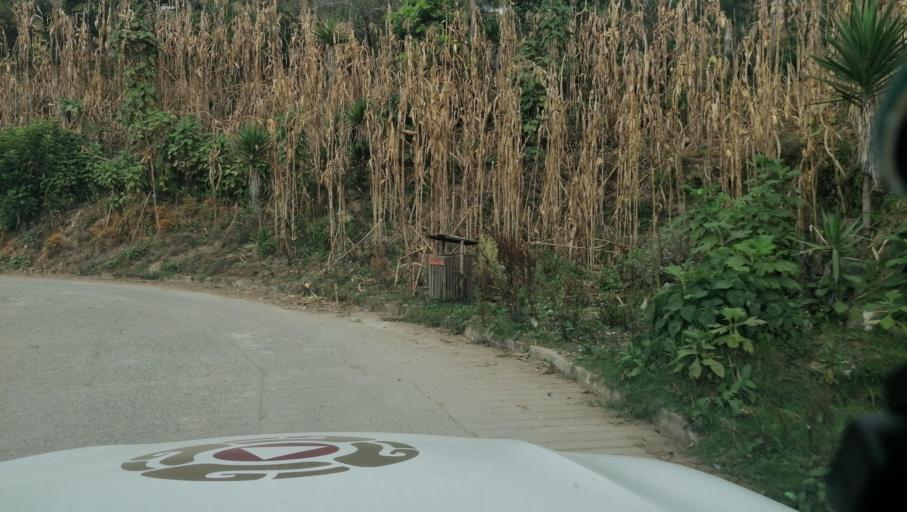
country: GT
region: San Marcos
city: Tacana
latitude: 15.2014
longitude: -92.1805
